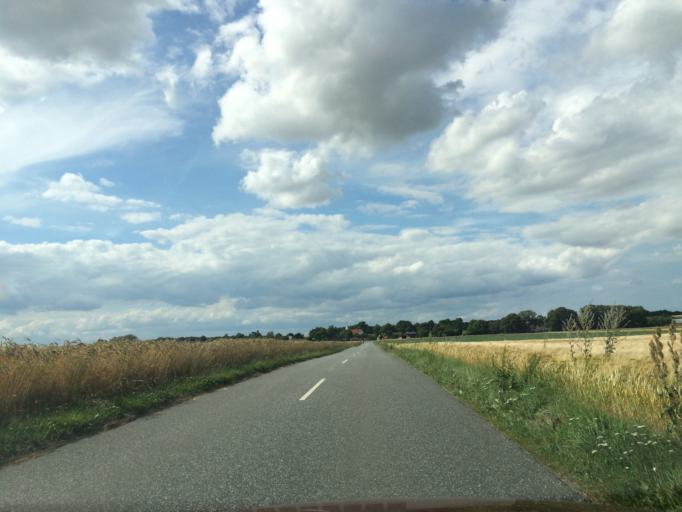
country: DK
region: Central Jutland
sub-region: Syddjurs Kommune
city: Ebeltoft
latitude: 56.2975
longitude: 10.7005
